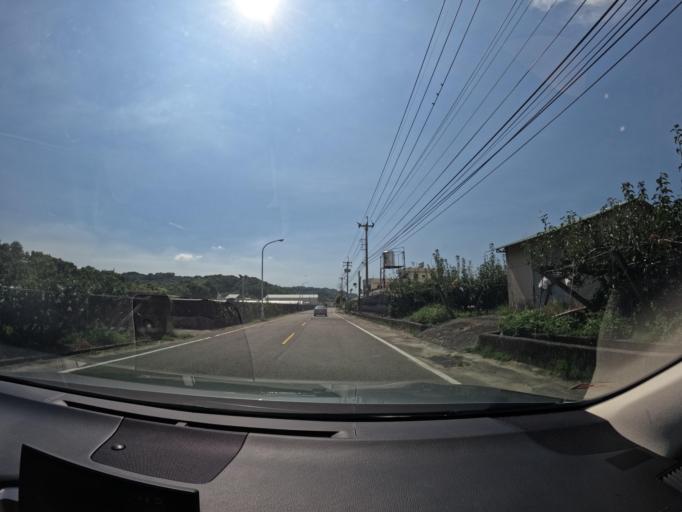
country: TW
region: Taiwan
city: Fengyuan
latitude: 24.3063
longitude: 120.8029
